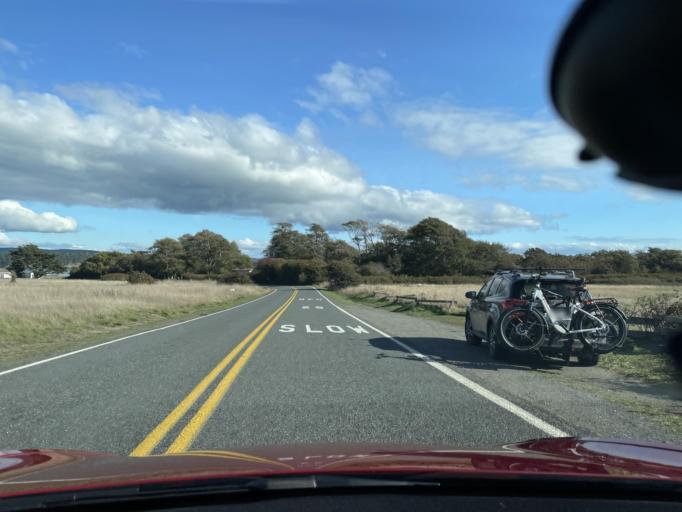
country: US
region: Washington
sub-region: San Juan County
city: Friday Harbor
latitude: 48.4529
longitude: -122.9666
